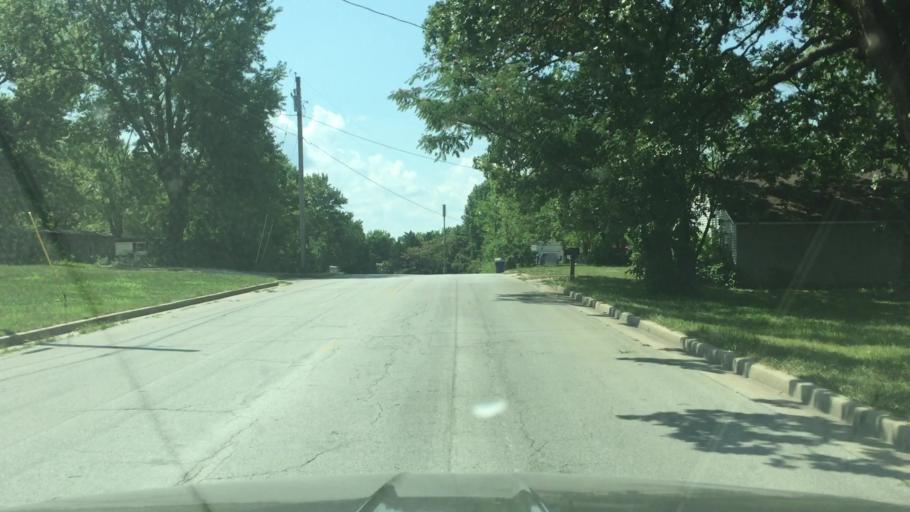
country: US
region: Missouri
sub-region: Miller County
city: Eldon
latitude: 38.3396
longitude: -92.5868
